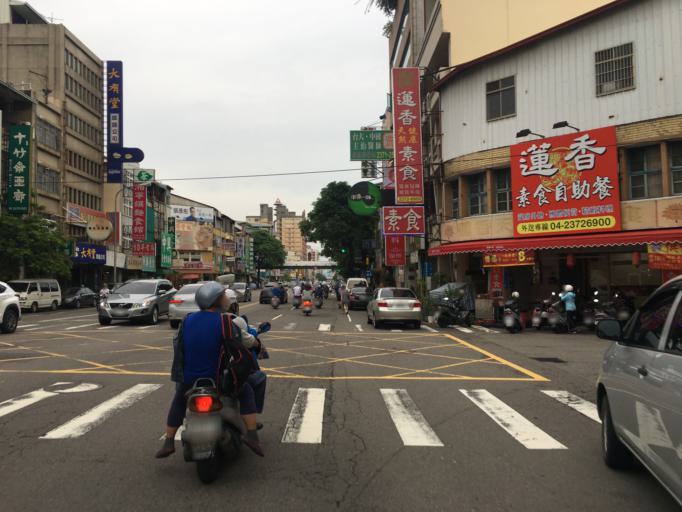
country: TW
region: Taiwan
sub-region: Taichung City
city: Taichung
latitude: 24.1402
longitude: 120.6676
